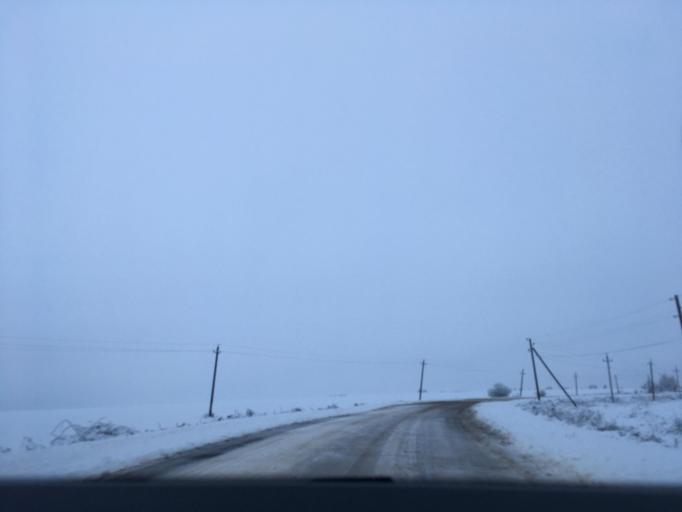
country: RU
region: Voronezj
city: Verkhniy Mamon
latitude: 50.0302
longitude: 40.0695
